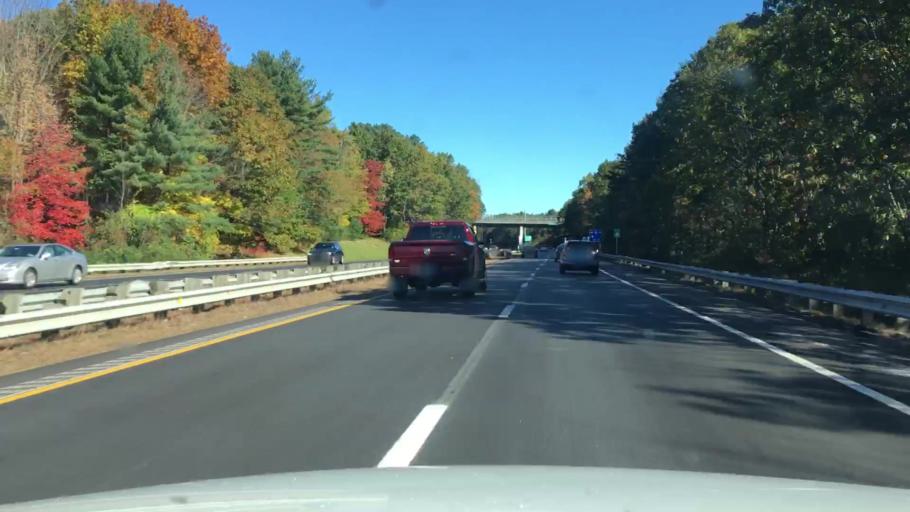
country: US
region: New Hampshire
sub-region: Strafford County
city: Dover
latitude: 43.2097
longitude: -70.8943
